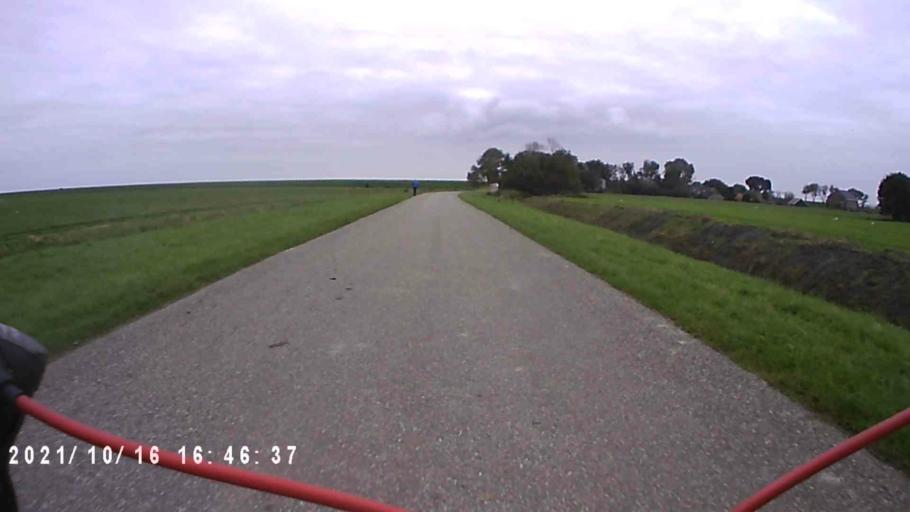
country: NL
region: Friesland
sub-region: Gemeente Dongeradeel
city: Anjum
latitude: 53.3619
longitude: 6.1460
